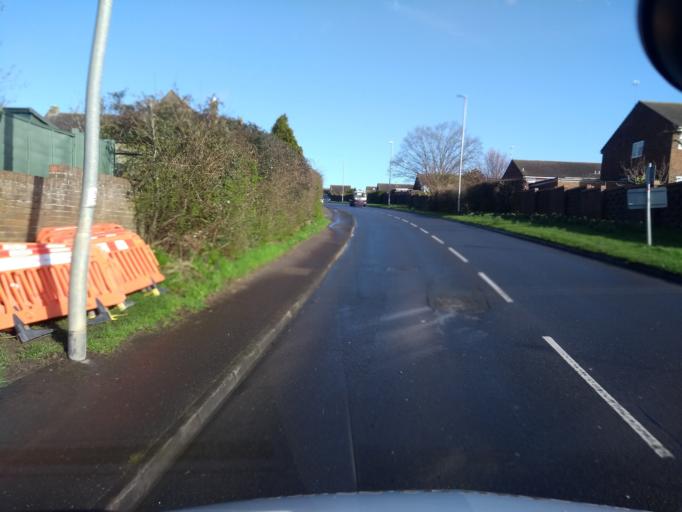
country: GB
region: England
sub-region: Somerset
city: Yeovil
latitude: 50.9556
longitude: -2.6100
